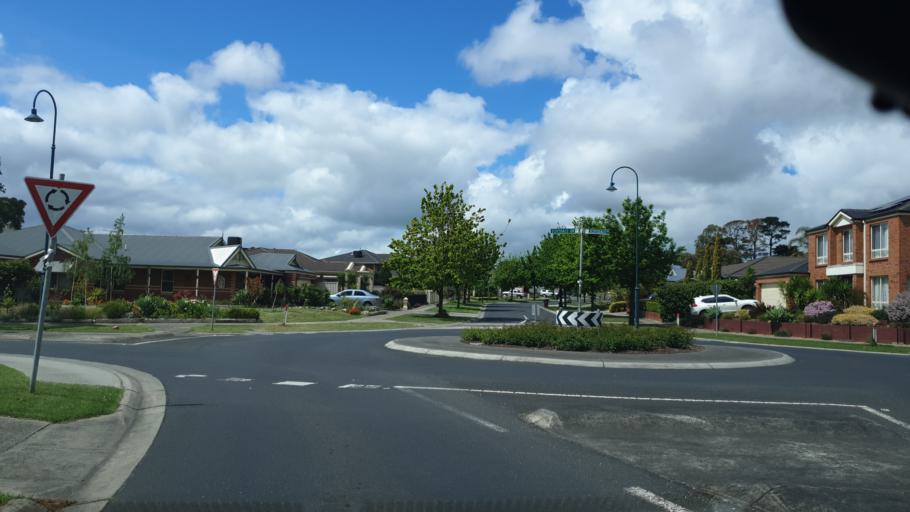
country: AU
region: Victoria
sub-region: Casey
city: Cranbourne East
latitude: -38.1045
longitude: 145.2960
